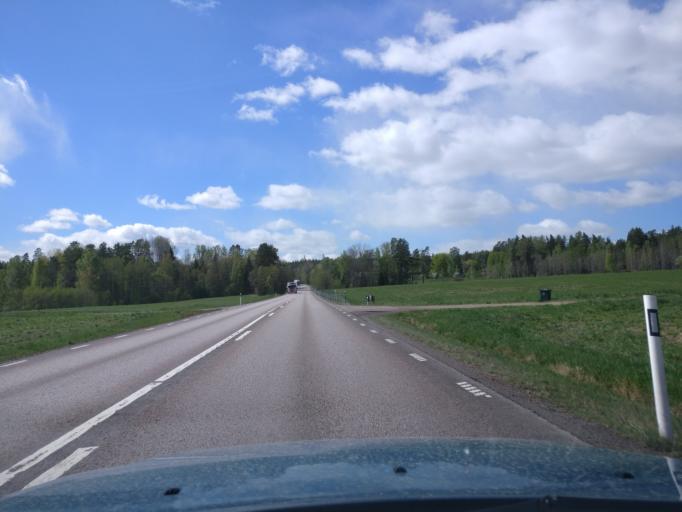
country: SE
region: Vaermland
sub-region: Karlstads Kommun
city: Molkom
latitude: 59.5929
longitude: 13.6967
